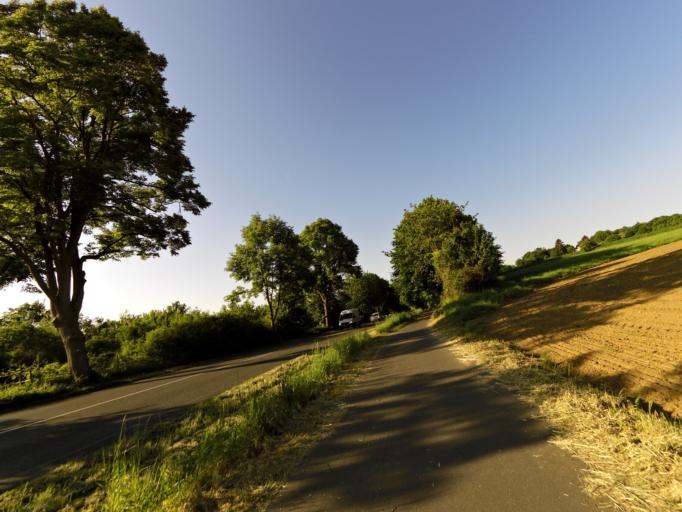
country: DE
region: North Rhine-Westphalia
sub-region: Regierungsbezirk Koln
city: Bonn
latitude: 50.7034
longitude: 7.0701
